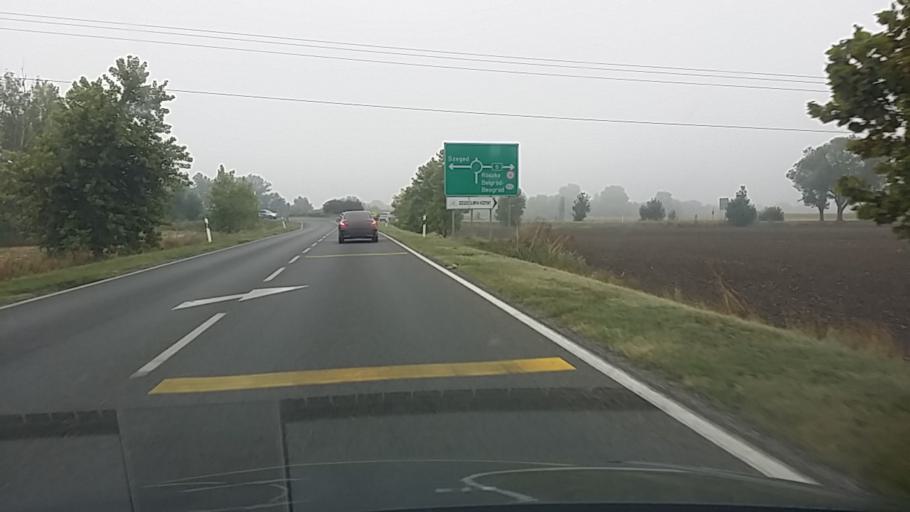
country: HU
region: Csongrad
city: Szeged
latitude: 46.2339
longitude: 20.0873
